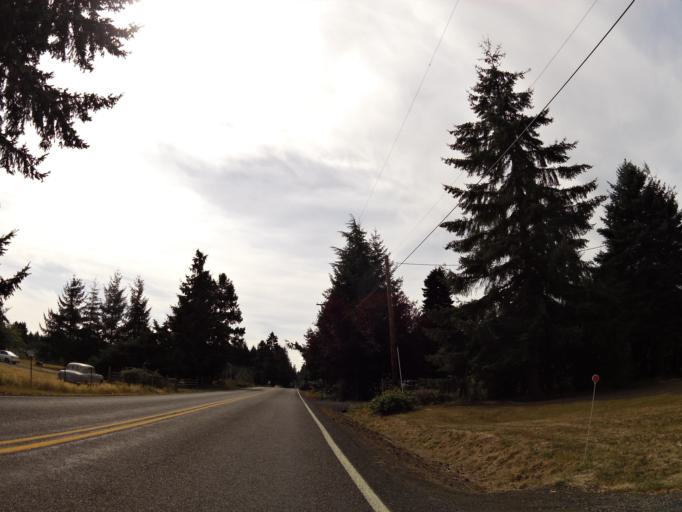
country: US
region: Washington
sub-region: Lewis County
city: Chehalis
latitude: 46.6004
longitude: -122.9712
